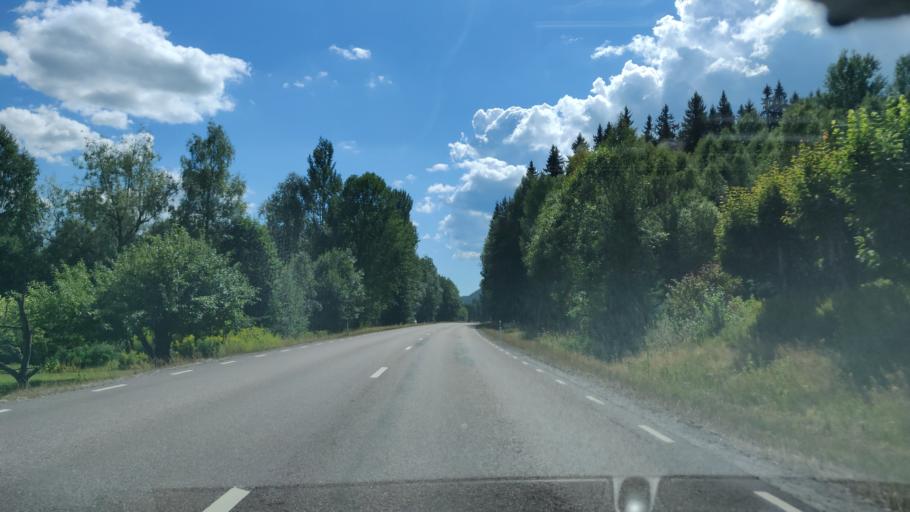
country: SE
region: Vaermland
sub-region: Hagfors Kommun
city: Ekshaerad
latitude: 60.1869
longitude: 13.4974
